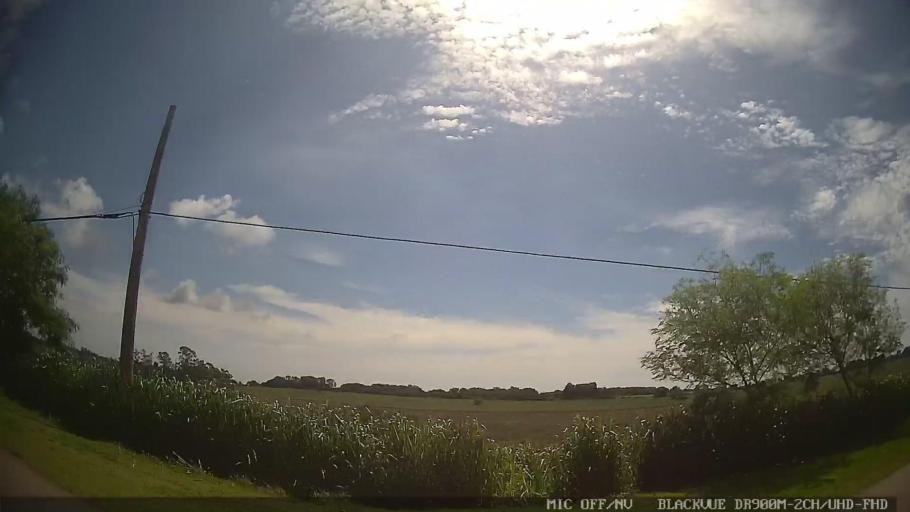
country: BR
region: Sao Paulo
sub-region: Tiete
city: Tiete
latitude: -23.1252
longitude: -47.6983
